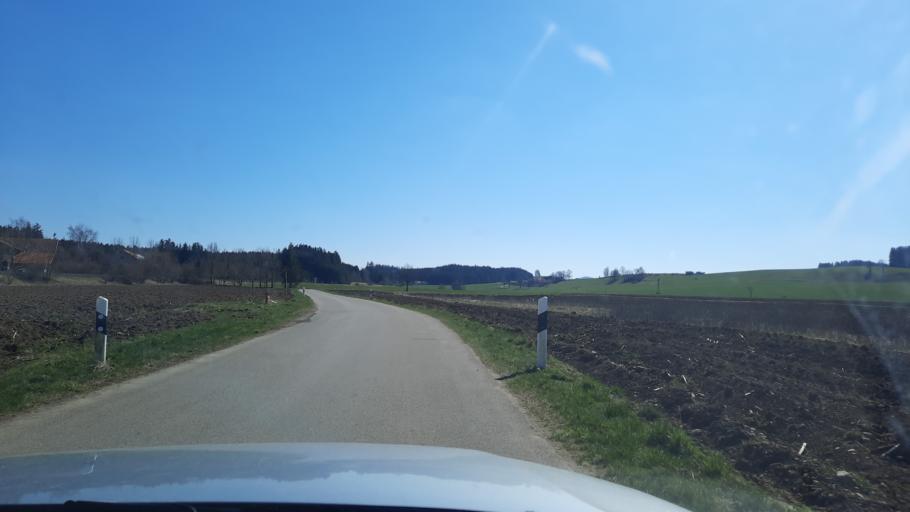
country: DE
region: Bavaria
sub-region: Swabia
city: Wolfertschwenden
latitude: 47.8521
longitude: 10.2542
